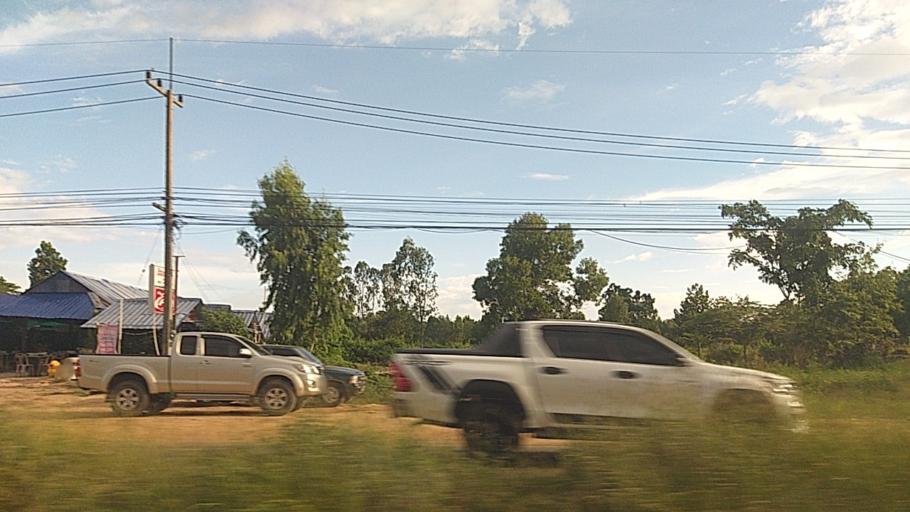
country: TH
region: Surin
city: Kap Choeng
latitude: 14.4554
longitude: 103.6816
